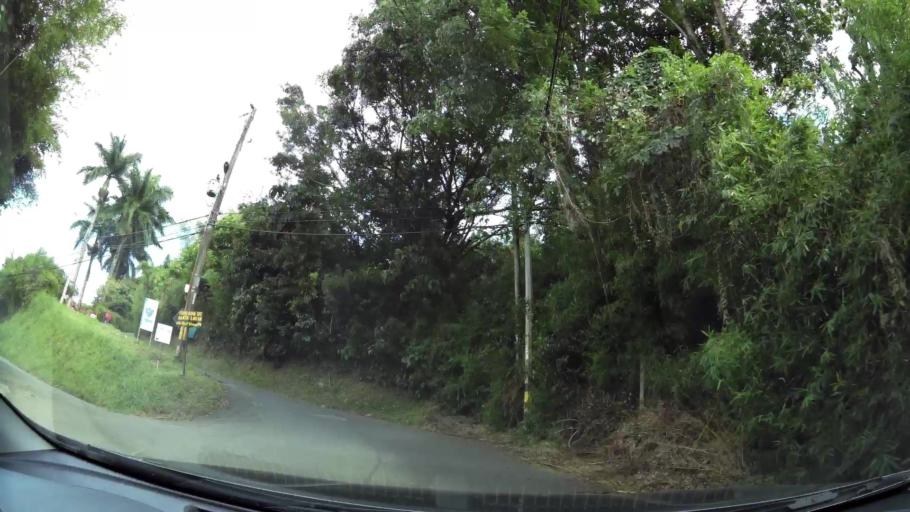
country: CO
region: Antioquia
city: Sabaneta
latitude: 6.1497
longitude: -75.6071
